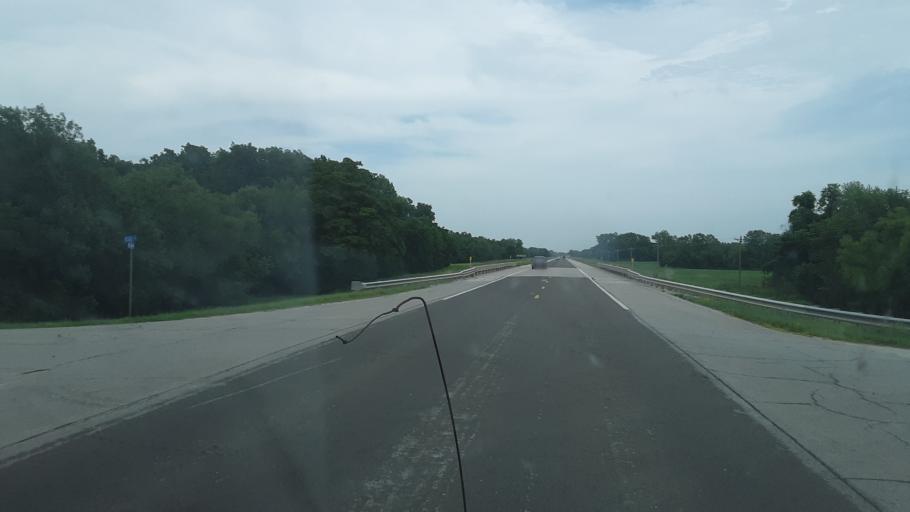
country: US
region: Kansas
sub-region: Allen County
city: Iola
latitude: 37.9220
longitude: -95.4467
